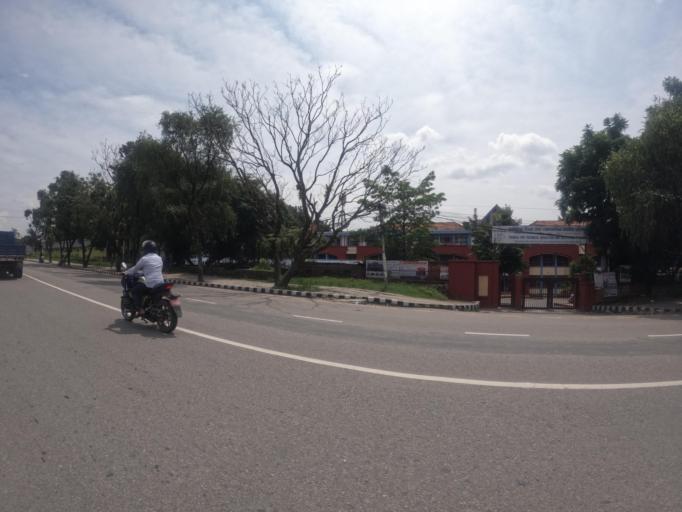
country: NP
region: Central Region
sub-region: Bagmati Zone
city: Bhaktapur
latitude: 27.6822
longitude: 85.3746
